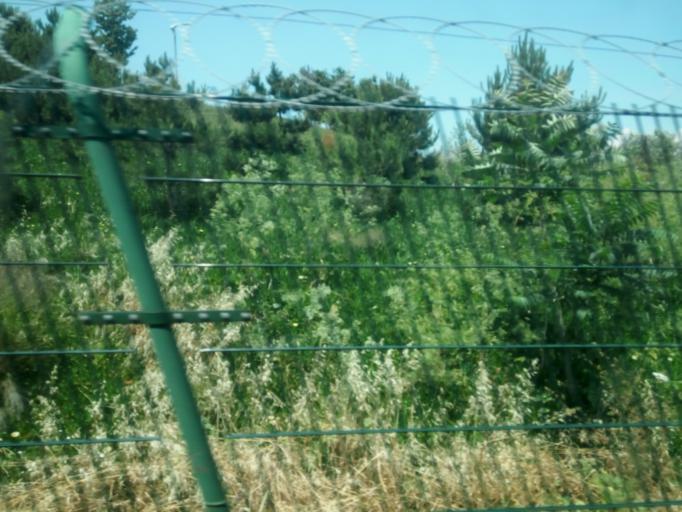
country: TR
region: Istanbul
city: guengoeren merter
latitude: 40.9969
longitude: 28.8777
